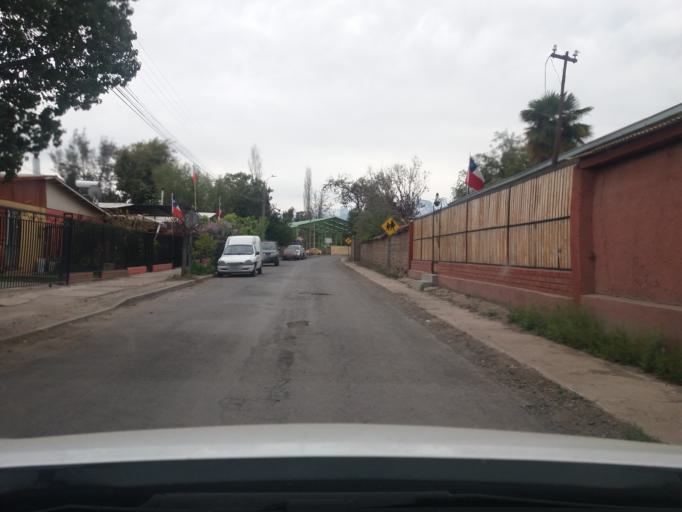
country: CL
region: Valparaiso
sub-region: Provincia de Los Andes
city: Los Andes
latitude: -32.8442
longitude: -70.6312
